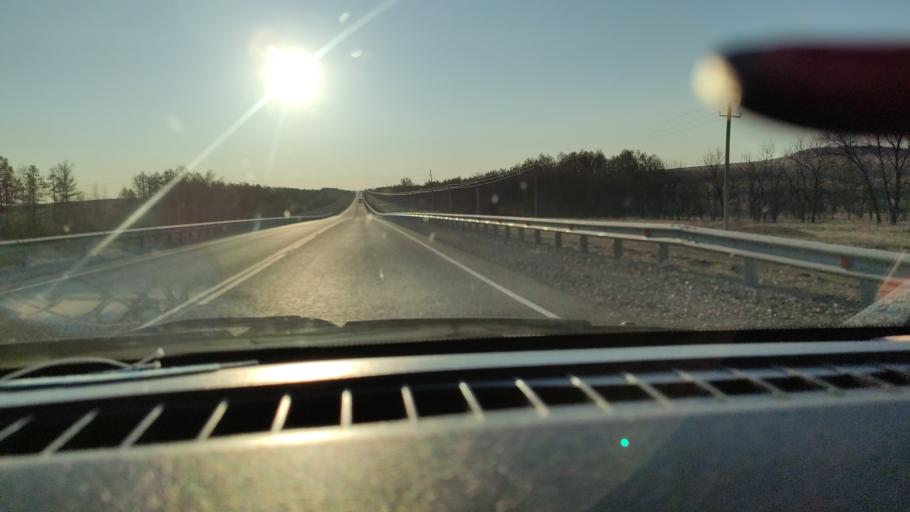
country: RU
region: Saratov
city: Shikhany
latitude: 52.1611
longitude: 47.1312
